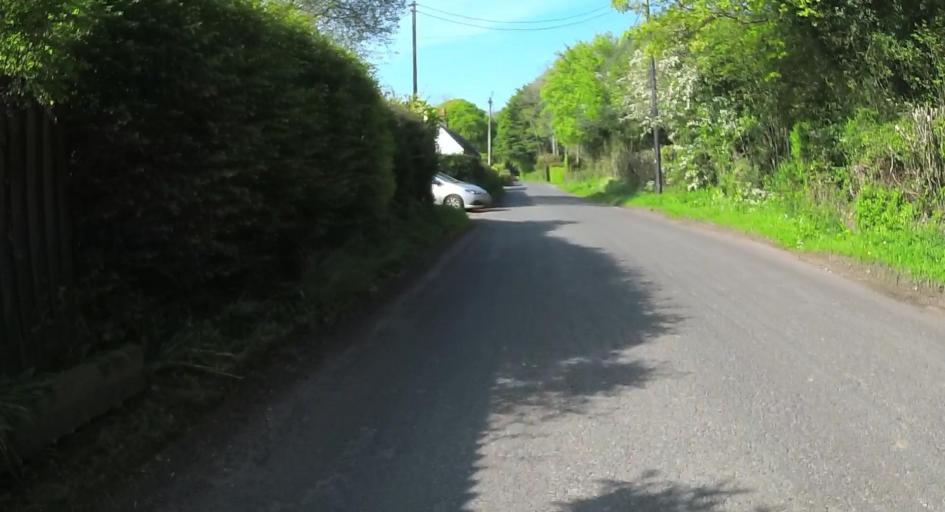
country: GB
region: England
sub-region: Hampshire
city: Four Marks
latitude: 51.1525
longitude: -1.0559
